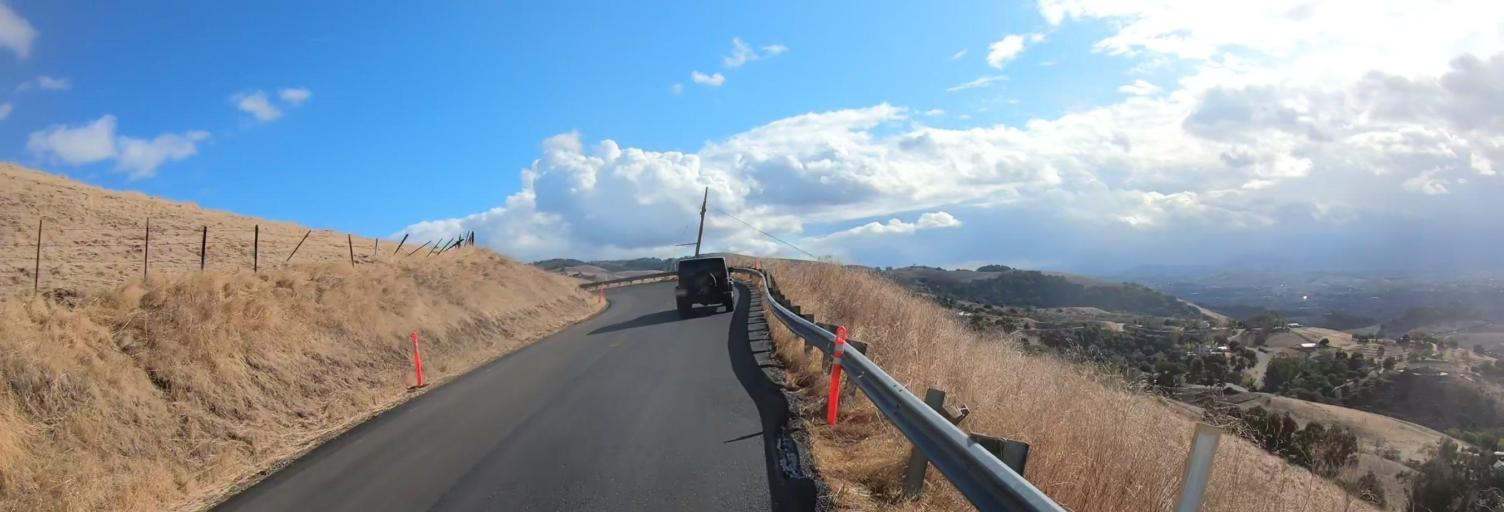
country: US
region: California
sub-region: Santa Clara County
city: East Foothills
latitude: 37.3725
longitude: -121.7716
